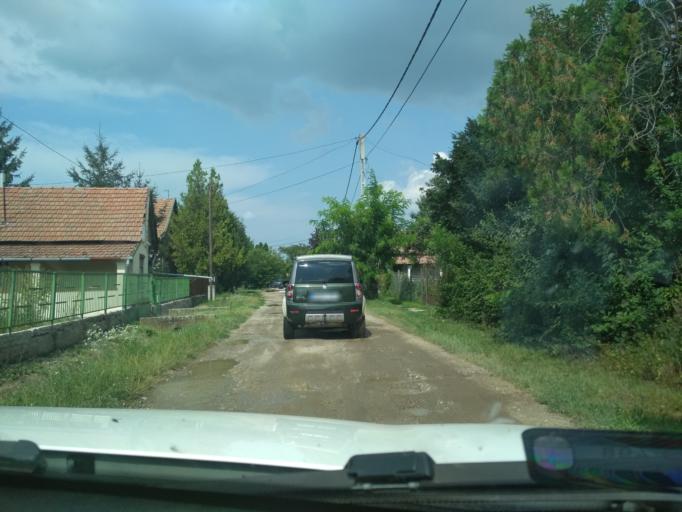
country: HU
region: Jasz-Nagykun-Szolnok
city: Abadszalok
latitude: 47.4771
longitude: 20.5875
